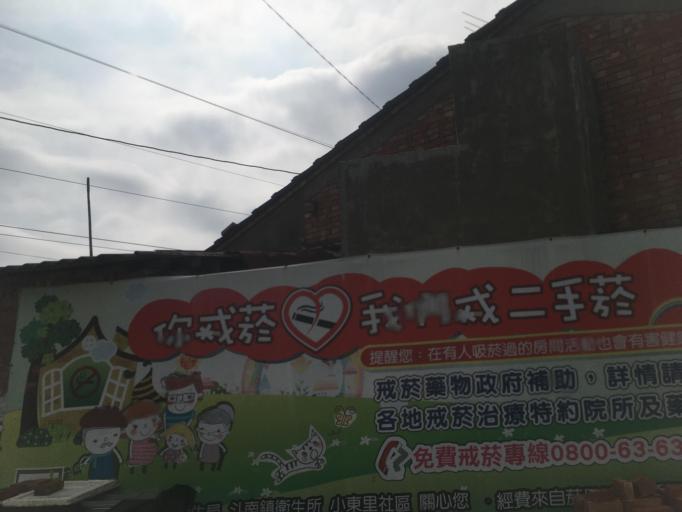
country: TW
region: Taiwan
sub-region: Yunlin
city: Douliu
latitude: 23.6897
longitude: 120.4678
